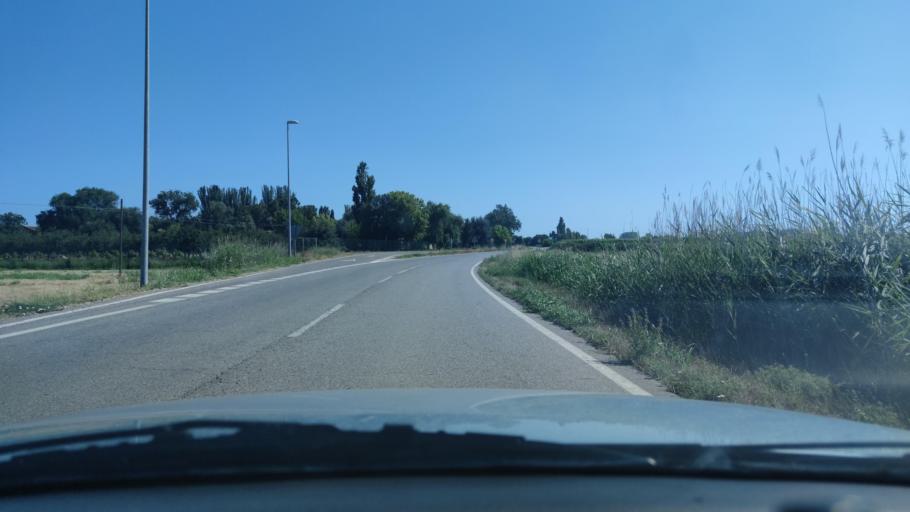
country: ES
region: Catalonia
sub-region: Provincia de Lleida
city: Bellvis
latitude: 41.6588
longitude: 0.8076
